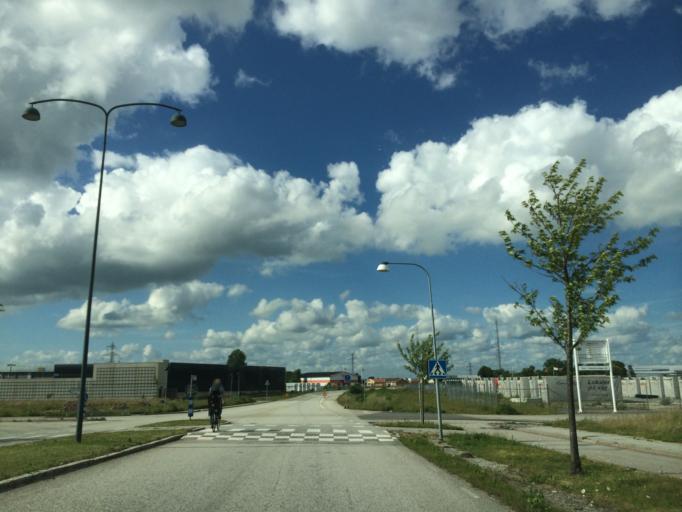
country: SE
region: Skane
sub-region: Lunds Kommun
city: Lund
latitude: 55.7201
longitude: 13.2290
